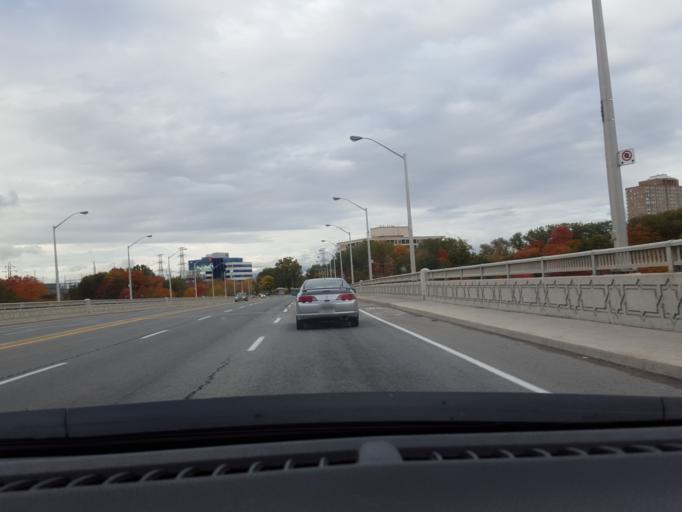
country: CA
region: Ontario
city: Toronto
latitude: 43.6986
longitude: -79.3501
